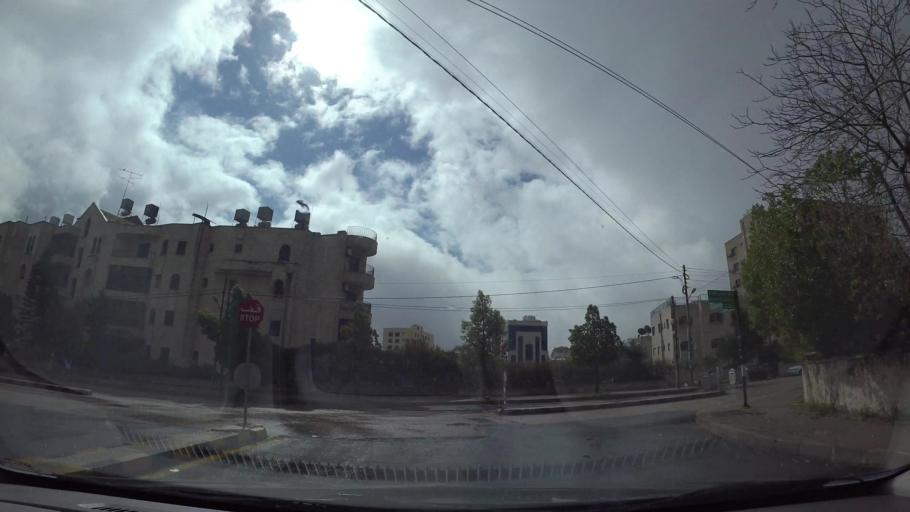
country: JO
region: Amman
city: Wadi as Sir
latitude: 31.9601
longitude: 35.8542
